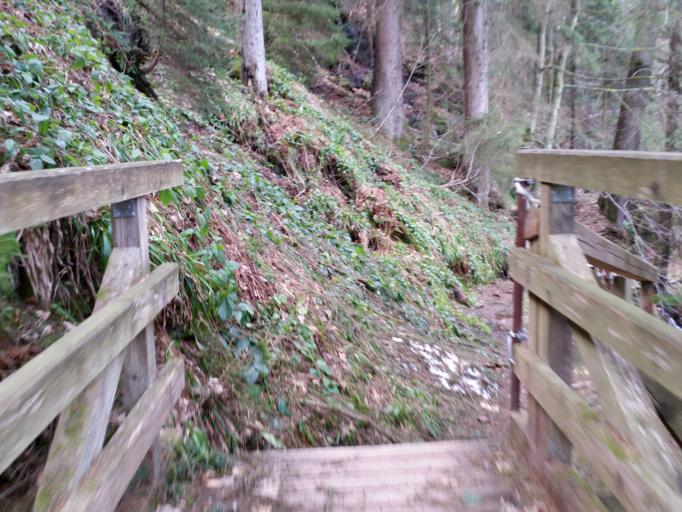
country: DE
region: Baden-Wuerttemberg
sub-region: Karlsruhe Region
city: Baiersbronn
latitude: 48.4846
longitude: 8.3333
